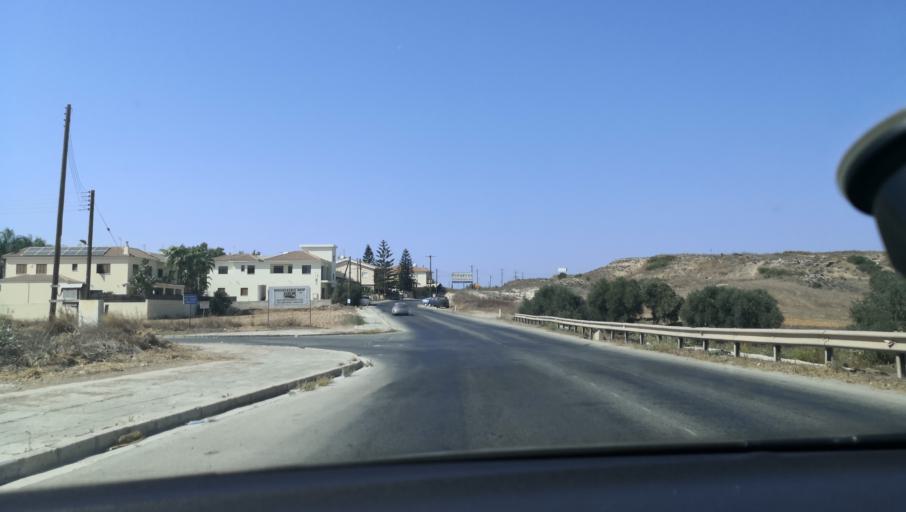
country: CY
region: Lefkosia
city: Kato Deftera
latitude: 35.1161
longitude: 33.2822
